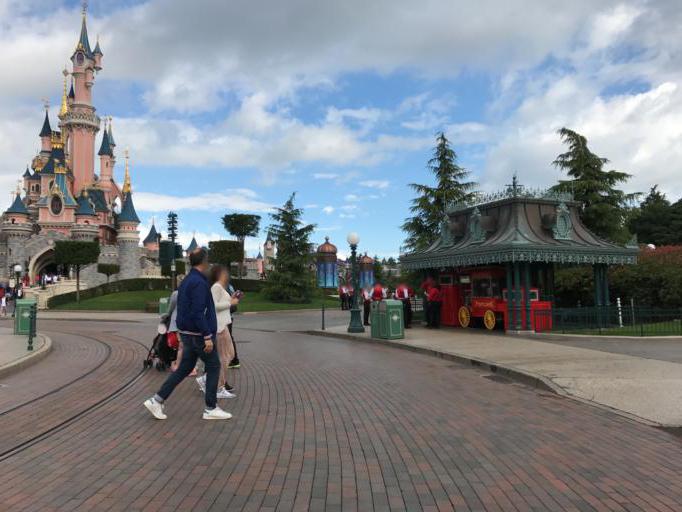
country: FR
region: Ile-de-France
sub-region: Departement de Seine-et-Marne
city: Chessy
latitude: 48.8727
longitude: 2.7771
